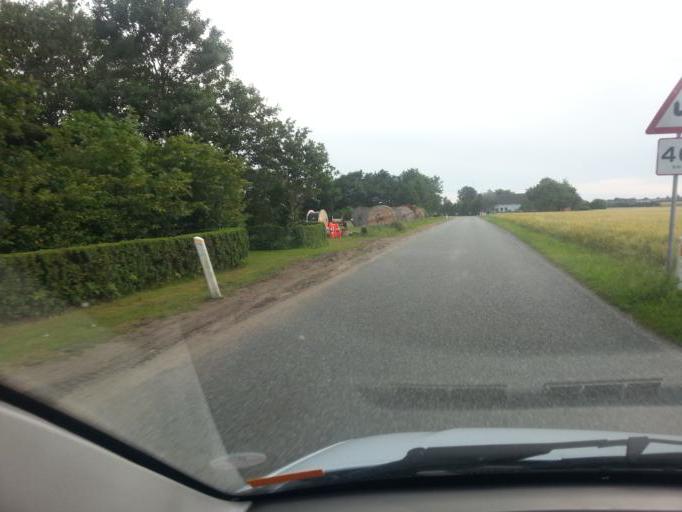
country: DK
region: South Denmark
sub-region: Vejen Kommune
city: Holsted
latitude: 55.4739
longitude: 8.8455
